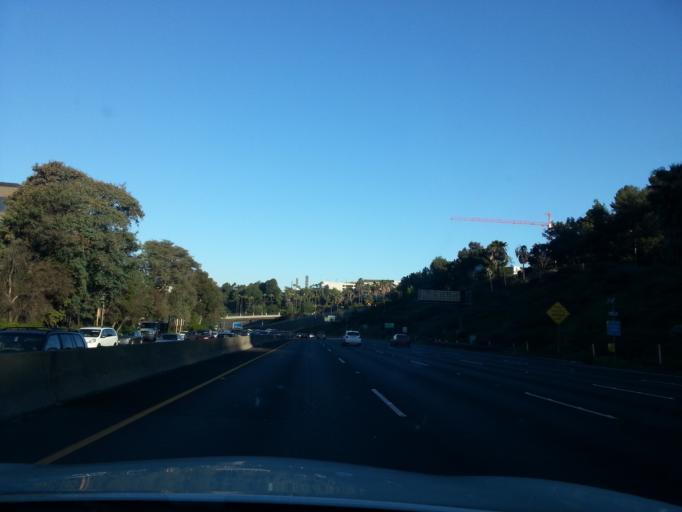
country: US
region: California
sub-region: Los Angeles County
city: Universal City
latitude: 34.1308
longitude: -118.3490
